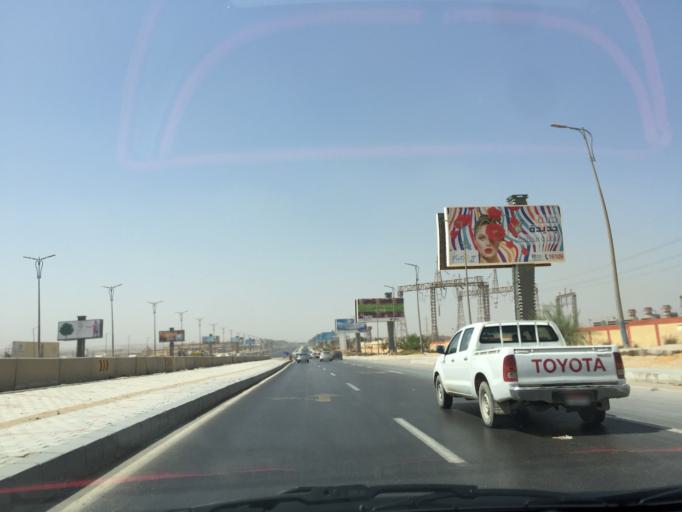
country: EG
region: Al Jizah
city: Awsim
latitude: 30.0510
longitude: 31.0464
